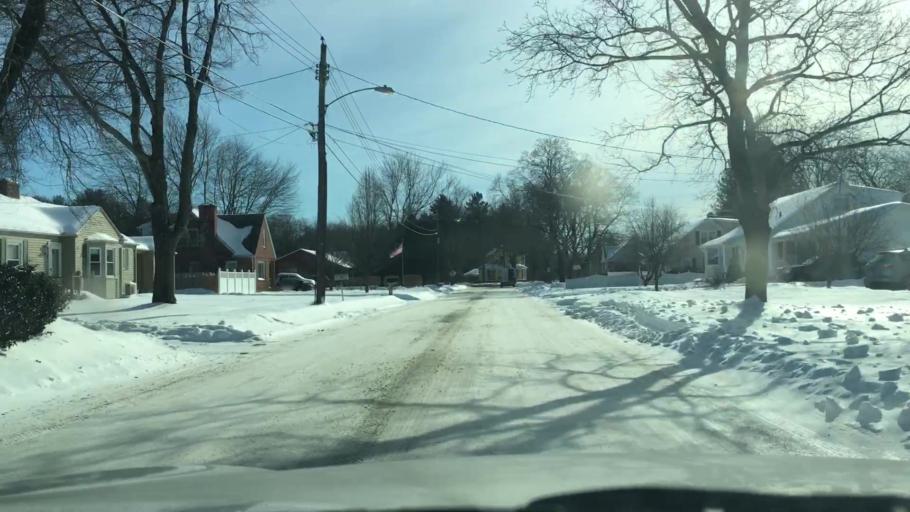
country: US
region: Massachusetts
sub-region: Hampden County
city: Agawam
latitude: 42.0718
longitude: -72.6557
